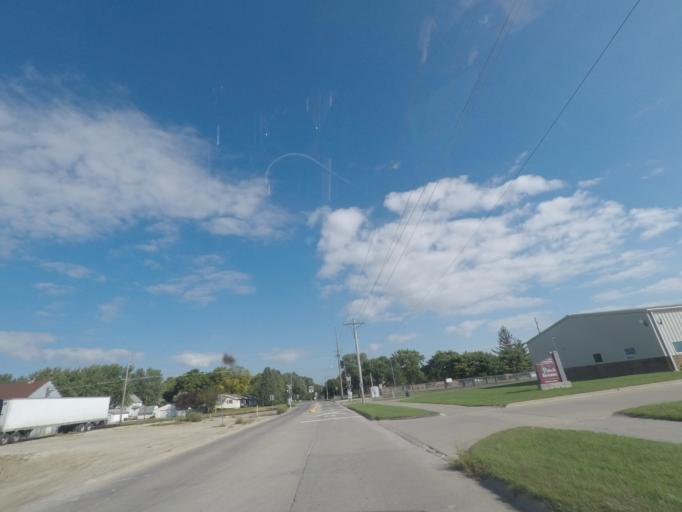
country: US
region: Iowa
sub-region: Story County
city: Nevada
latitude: 42.0146
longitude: -93.4445
